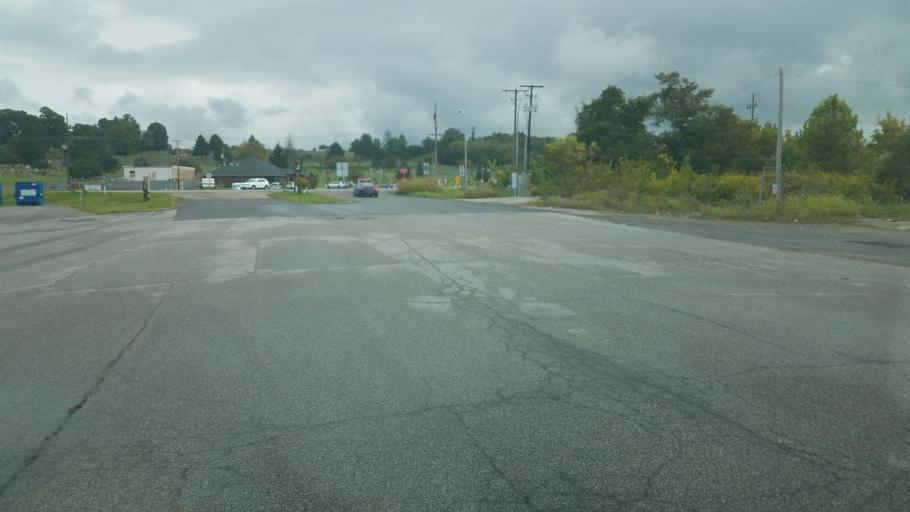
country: US
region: Ohio
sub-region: Scioto County
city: Wheelersburg
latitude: 38.7121
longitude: -82.8568
